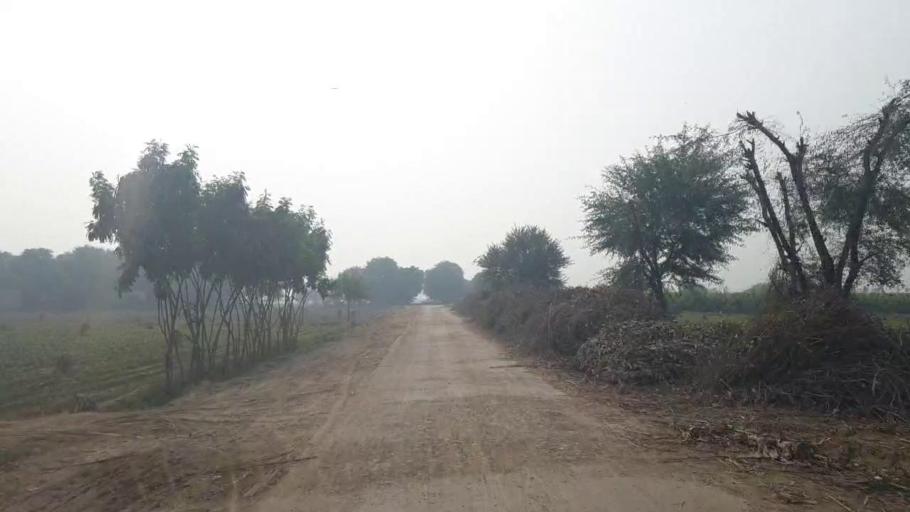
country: PK
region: Sindh
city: Tando Adam
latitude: 25.7129
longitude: 68.6263
